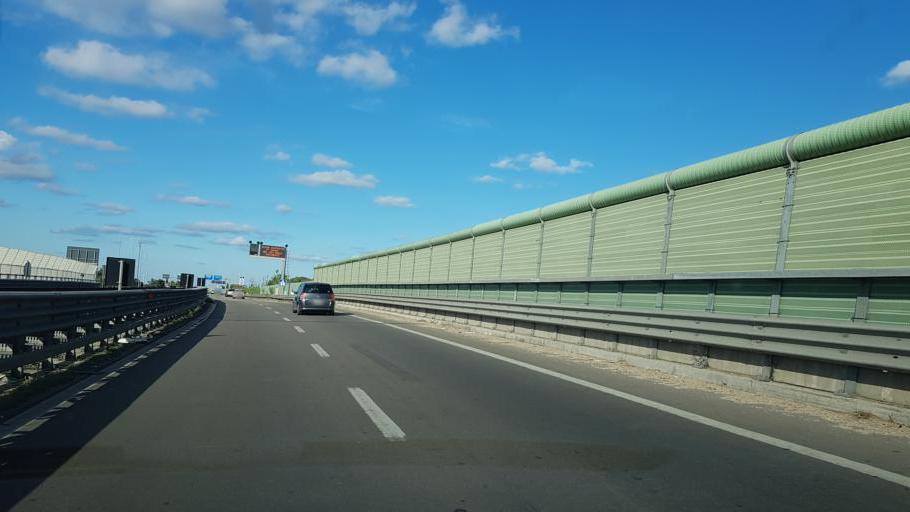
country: IT
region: Apulia
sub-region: Provincia di Lecce
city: Giorgilorio
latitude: 40.3605
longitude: 18.1414
